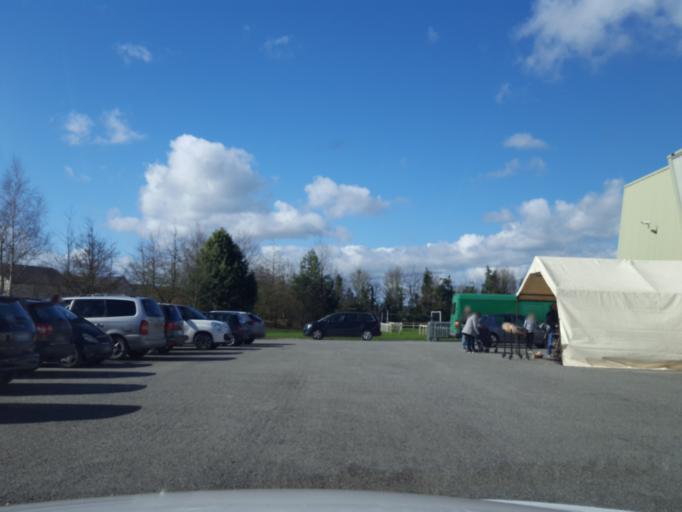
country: FR
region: Brittany
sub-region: Departement d'Ille-et-Vilaine
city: Chavagne
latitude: 48.0538
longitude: -1.7942
